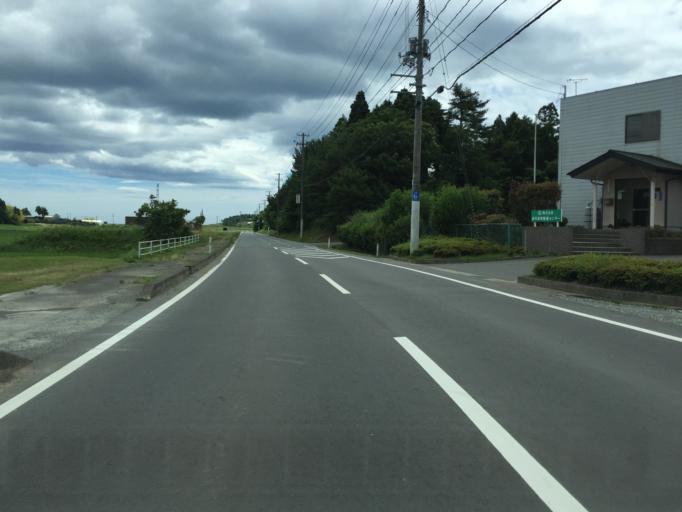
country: JP
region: Fukushima
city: Namie
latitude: 37.6651
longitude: 141.0018
